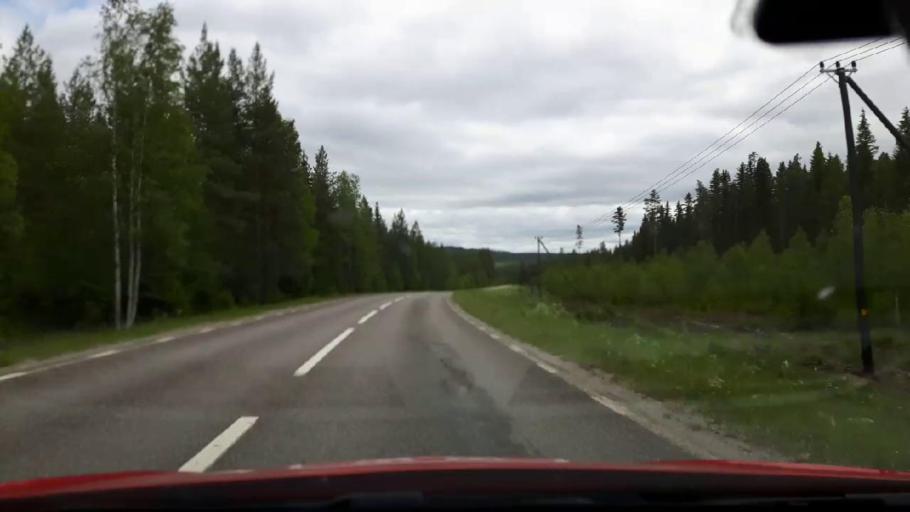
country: SE
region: Jaemtland
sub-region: Ragunda Kommun
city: Hammarstrand
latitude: 63.0783
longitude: 16.3735
